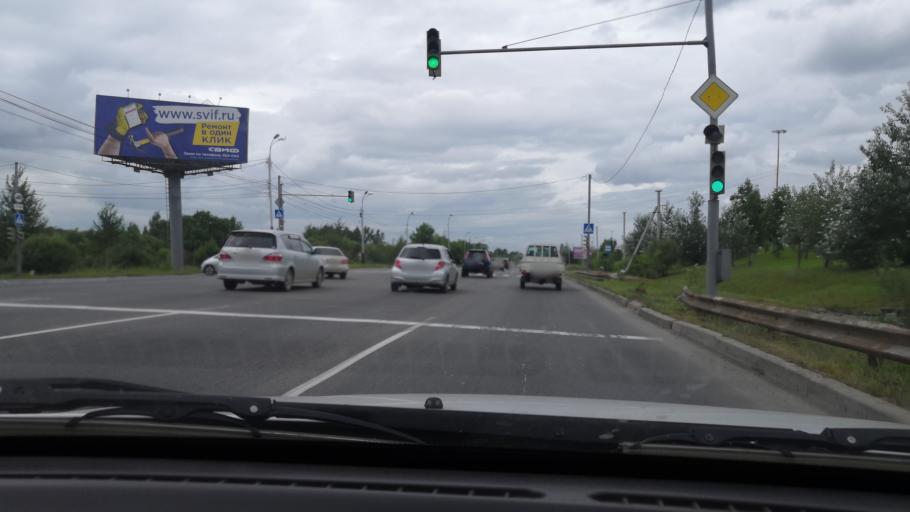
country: RU
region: Khabarovsk Krai
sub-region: Khabarovskiy Rayon
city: Khabarovsk
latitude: 48.5371
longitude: 135.0673
